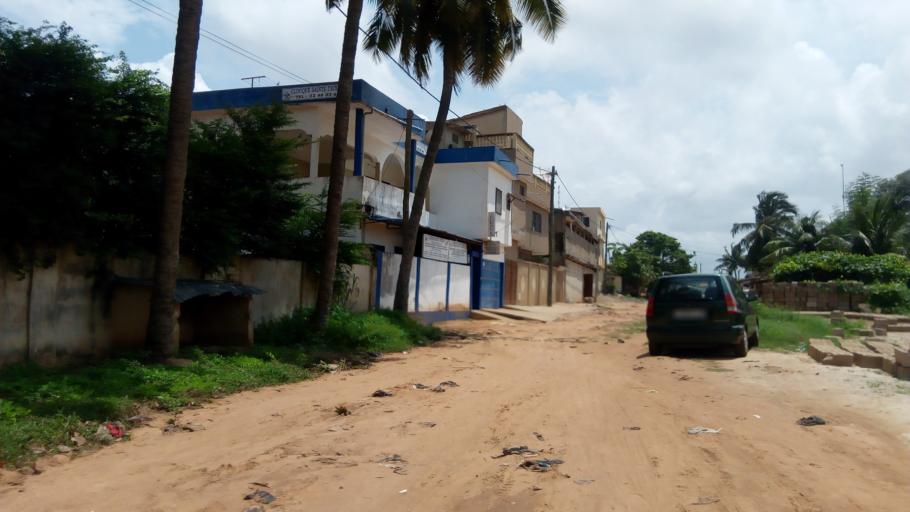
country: TG
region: Maritime
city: Lome
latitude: 6.1816
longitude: 1.1722
